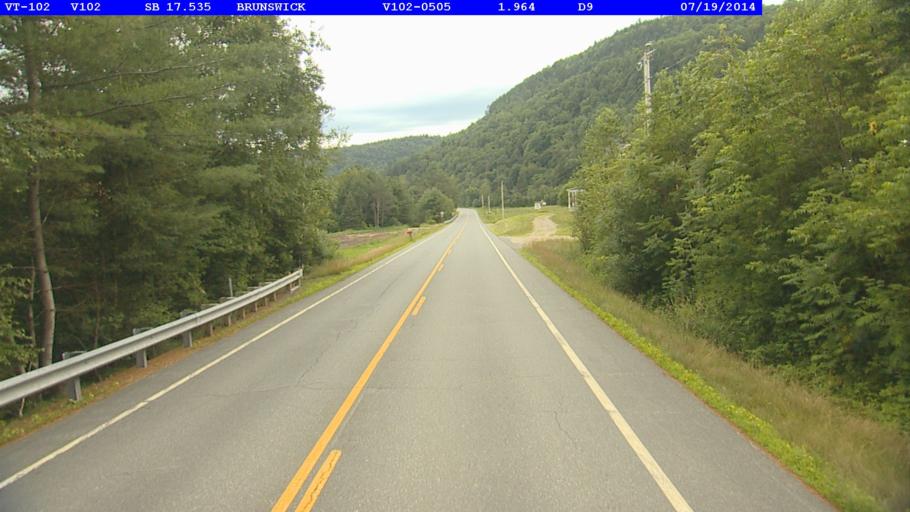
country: US
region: New Hampshire
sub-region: Coos County
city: Stratford
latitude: 44.6880
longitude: -71.5996
